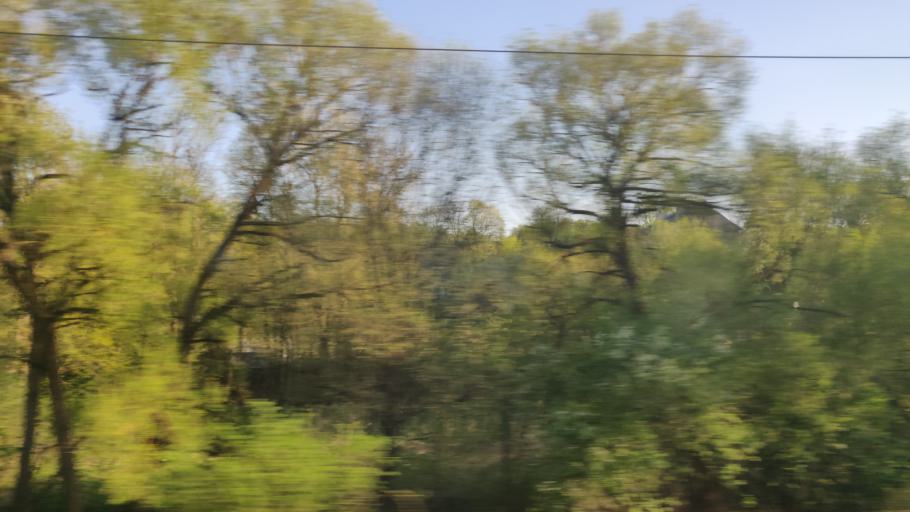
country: LT
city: Grigiskes
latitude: 54.6332
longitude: 25.1044
